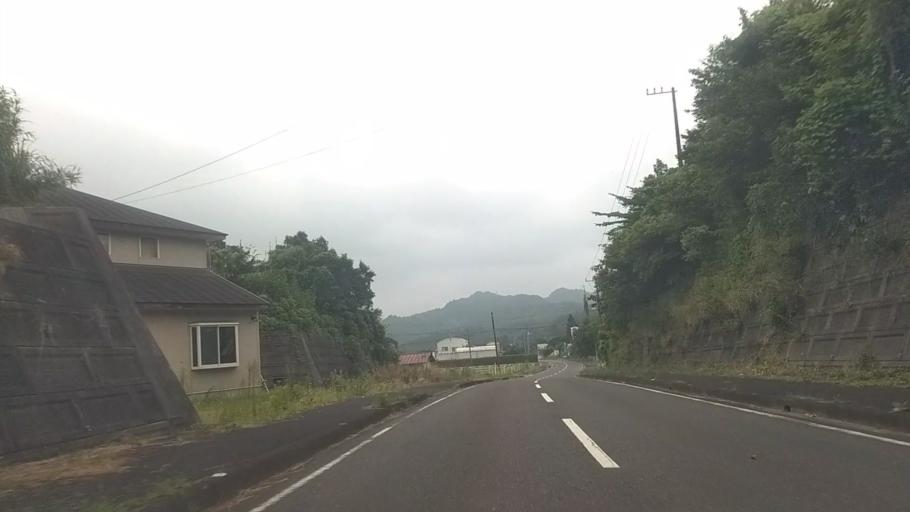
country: JP
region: Chiba
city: Kawaguchi
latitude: 35.2340
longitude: 140.0863
